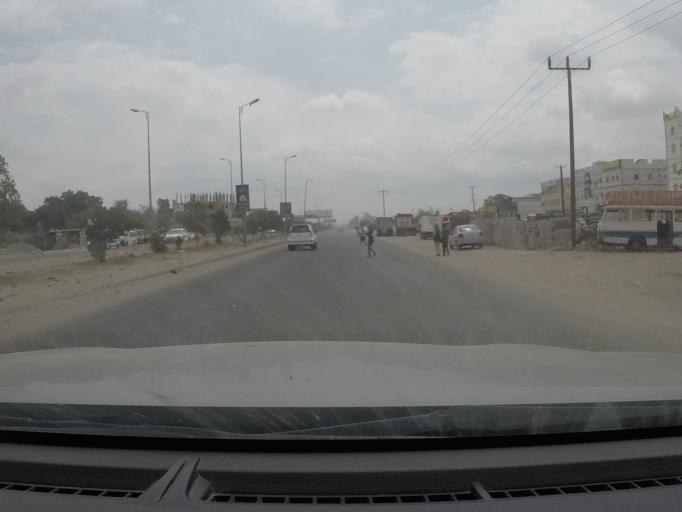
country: YE
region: Lahij
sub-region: Al  Hawtah
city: Lahij
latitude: 12.9963
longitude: 44.9215
